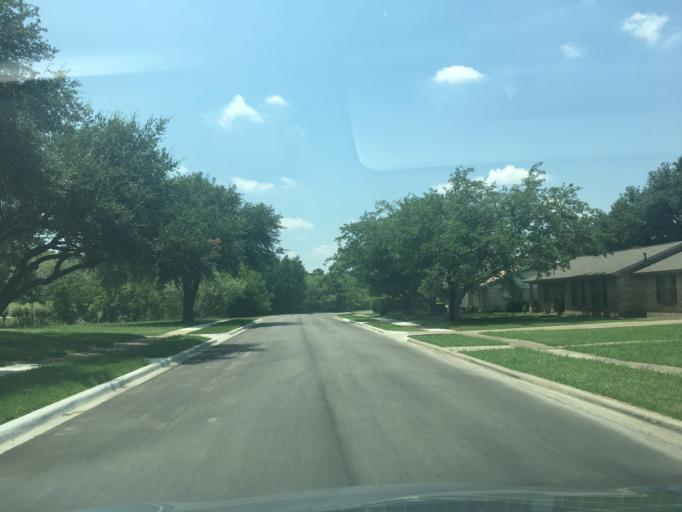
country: US
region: Texas
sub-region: Dallas County
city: Carrollton
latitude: 32.9358
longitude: -96.8725
